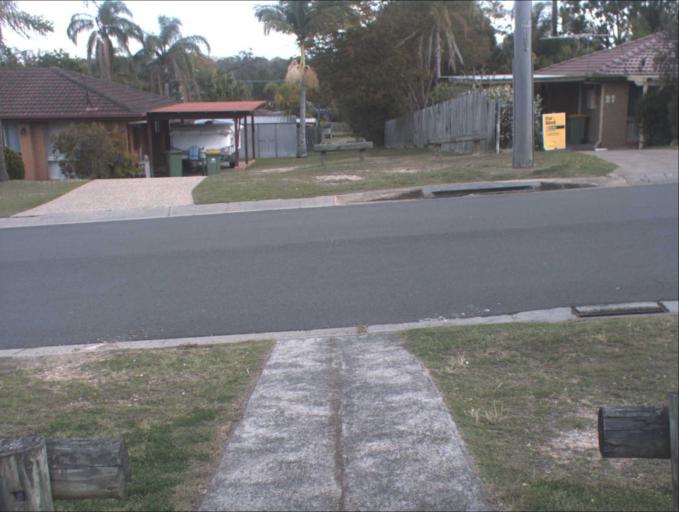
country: AU
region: Queensland
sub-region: Logan
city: Park Ridge South
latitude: -27.6694
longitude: 153.0429
